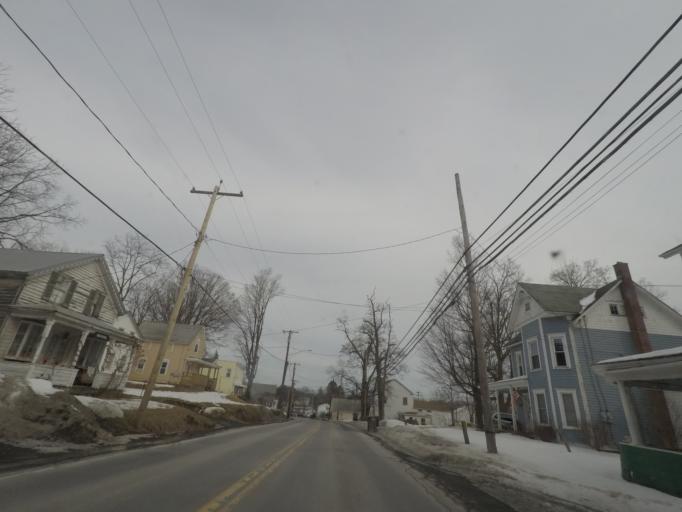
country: US
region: New York
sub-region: Albany County
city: Voorheesville
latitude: 42.5759
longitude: -73.9651
